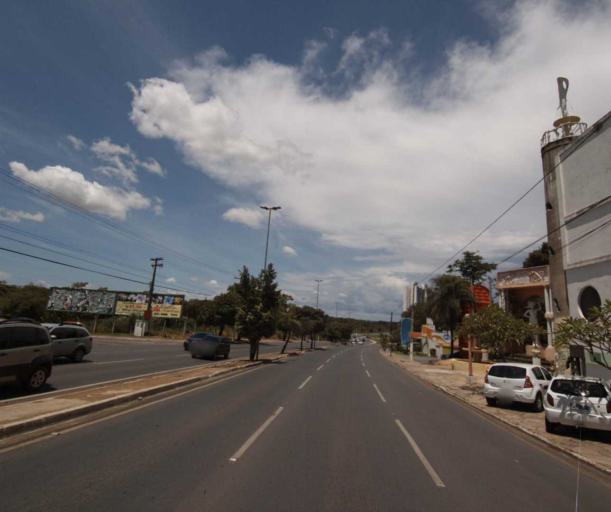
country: BR
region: Mato Grosso
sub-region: Cuiaba
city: Cuiaba
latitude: -15.5781
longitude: -56.1091
